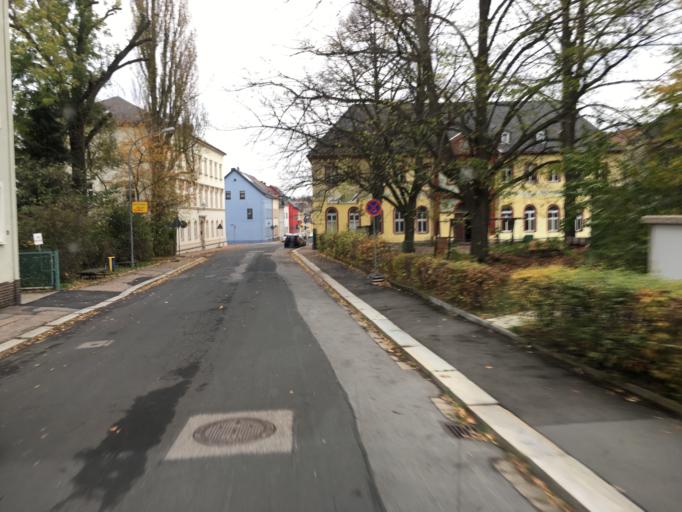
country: DE
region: Saxony
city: Hainichen
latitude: 50.9718
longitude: 13.1189
